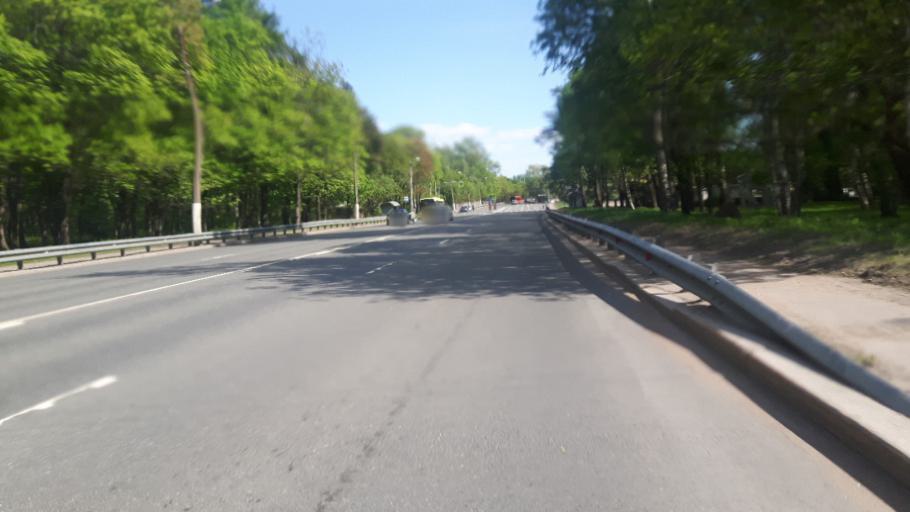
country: RU
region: Leningrad
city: Vyborg
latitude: 60.7289
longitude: 28.7014
